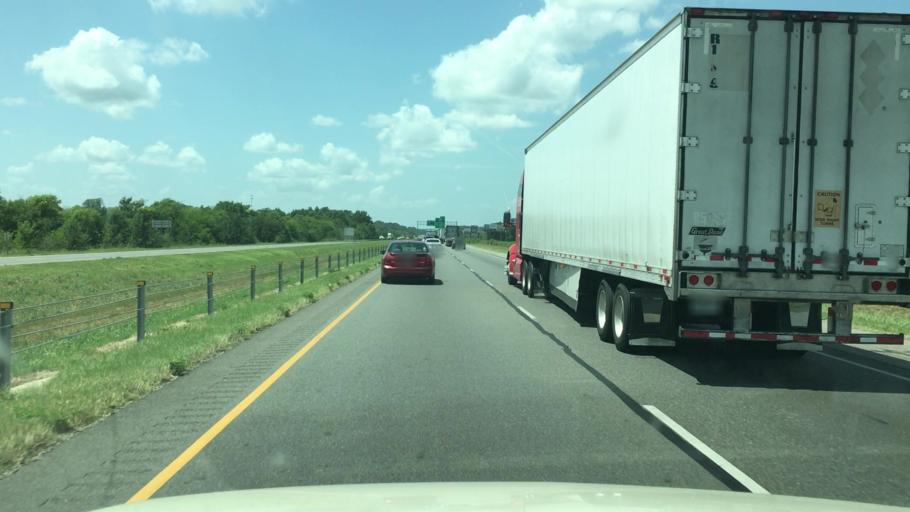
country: US
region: Arkansas
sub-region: Miller County
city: Texarkana
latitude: 33.5058
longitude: -93.9516
